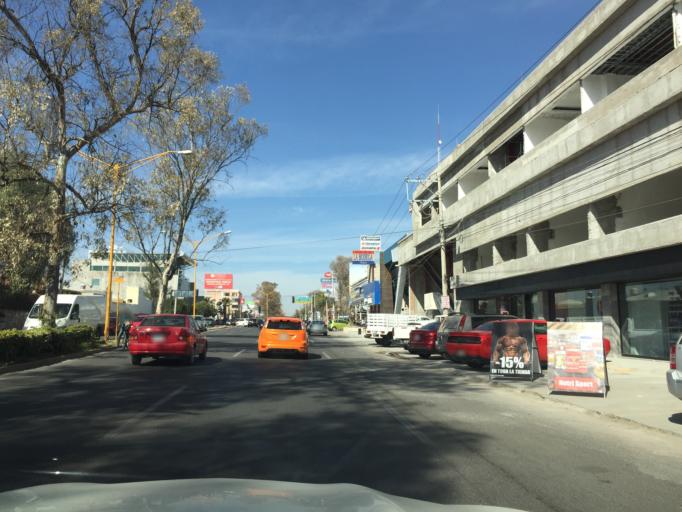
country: MX
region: Aguascalientes
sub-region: Jesus Maria
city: El Llano
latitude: 21.9188
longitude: -102.2976
